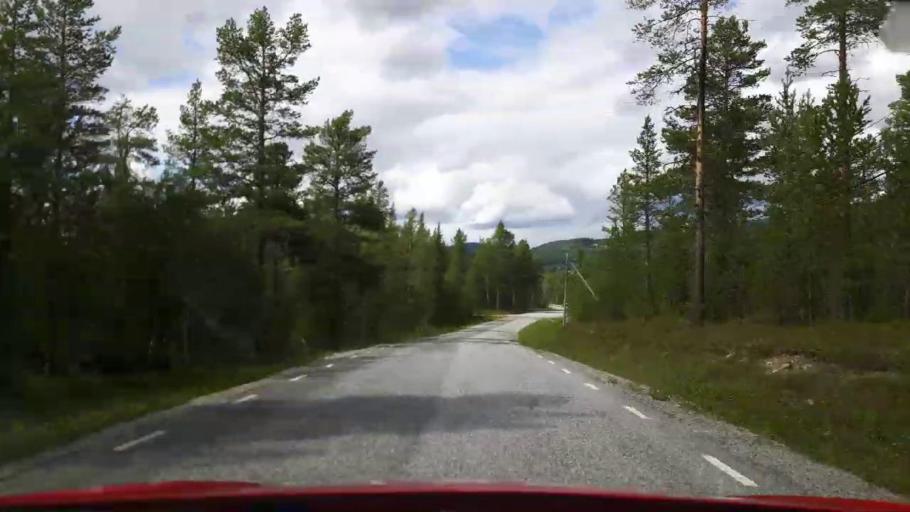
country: NO
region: Hedmark
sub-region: Engerdal
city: Engerdal
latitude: 62.4235
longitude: 12.6891
